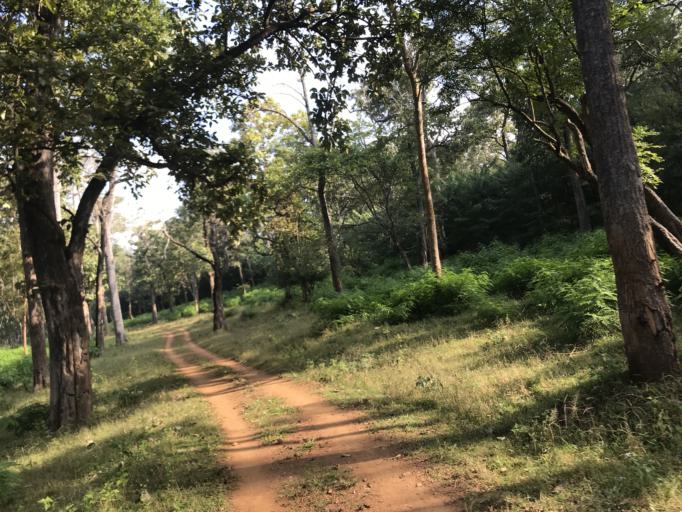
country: IN
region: Karnataka
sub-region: Mysore
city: Heggadadevankote
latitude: 11.9425
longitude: 76.2012
